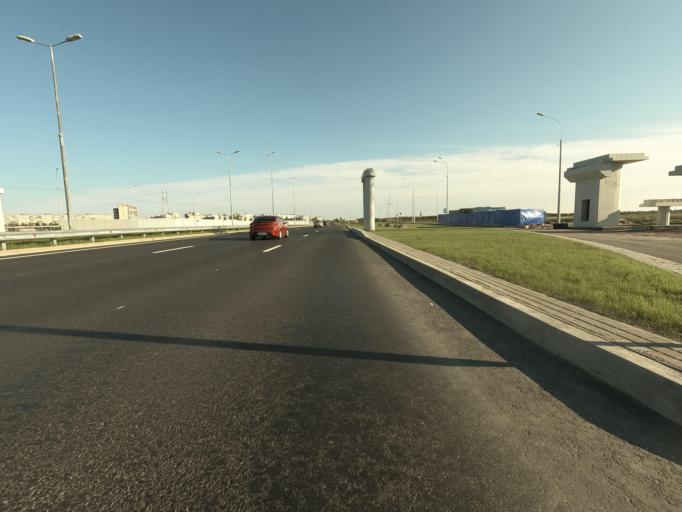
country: RU
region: St.-Petersburg
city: Kolpino
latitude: 59.7401
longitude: 30.5485
